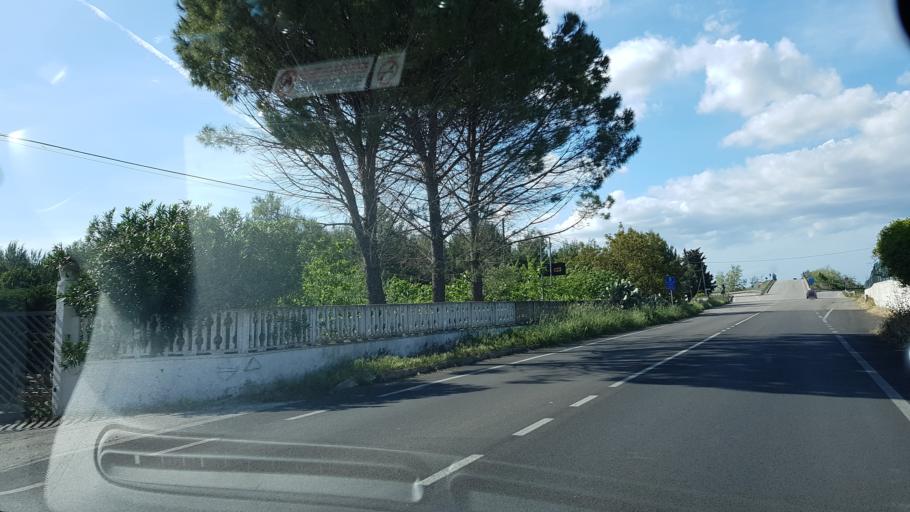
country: IT
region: Apulia
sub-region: Provincia di Brindisi
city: Mesagne
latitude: 40.5649
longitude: 17.7868
